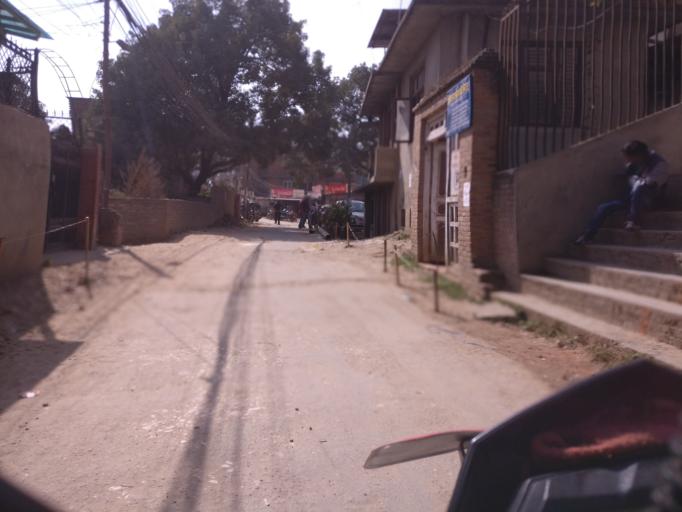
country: NP
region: Central Region
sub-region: Bagmati Zone
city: Patan
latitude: 27.6658
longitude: 85.3245
